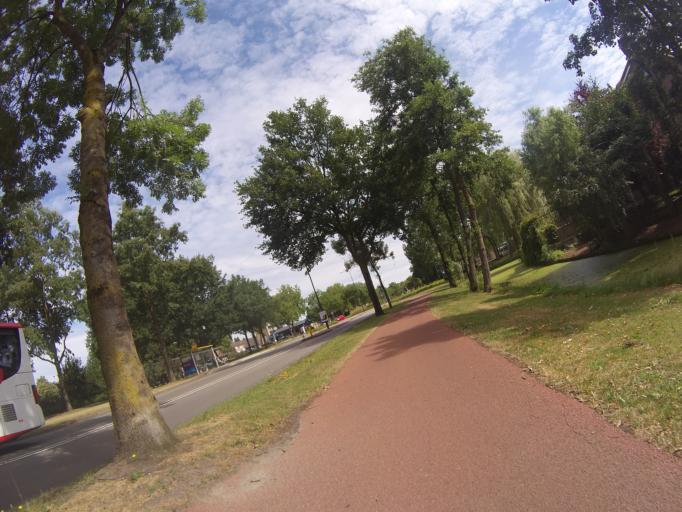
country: NL
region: Utrecht
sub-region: Gemeente Bunschoten
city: Spakenburg
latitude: 52.2461
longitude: 5.3682
